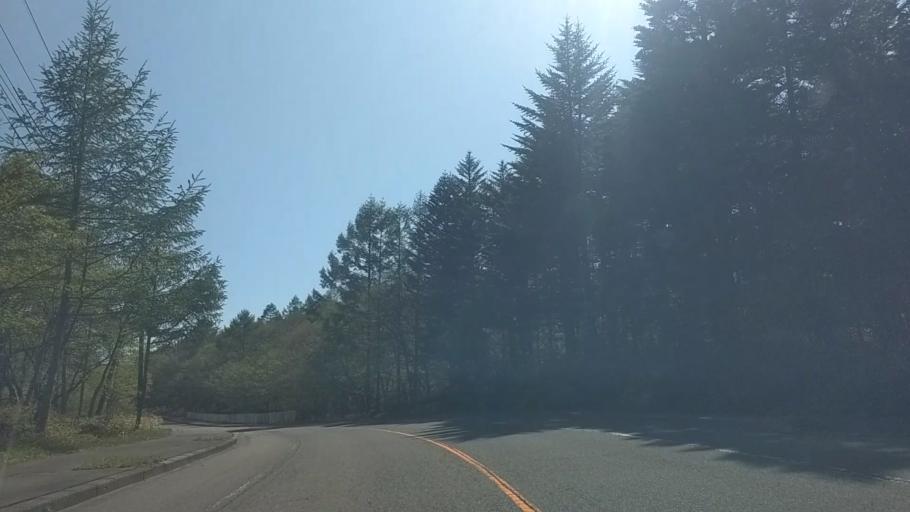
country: JP
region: Yamanashi
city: Nirasaki
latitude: 35.9416
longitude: 138.4357
